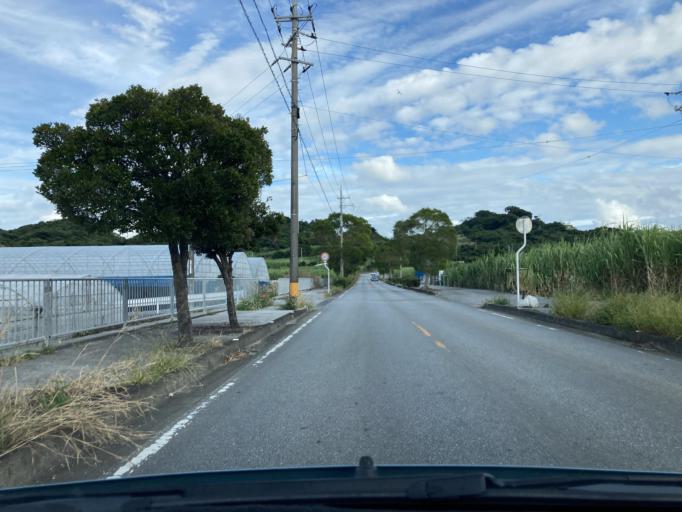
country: JP
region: Okinawa
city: Itoman
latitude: 26.1353
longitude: 127.7187
